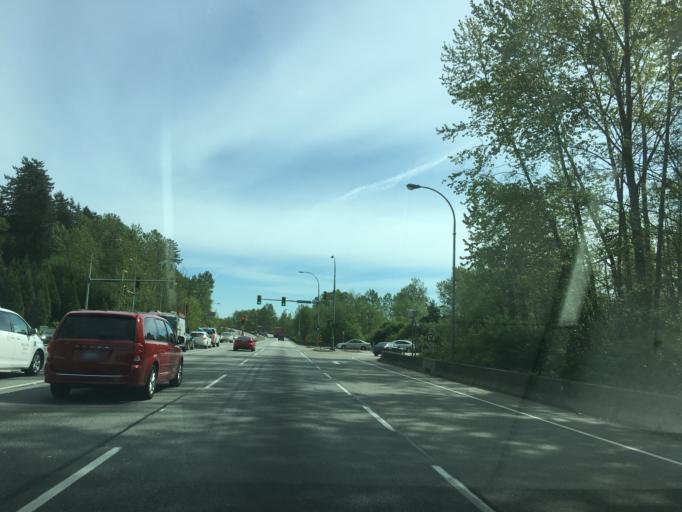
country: CA
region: British Columbia
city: Coquitlam
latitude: 49.2273
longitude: -122.7968
